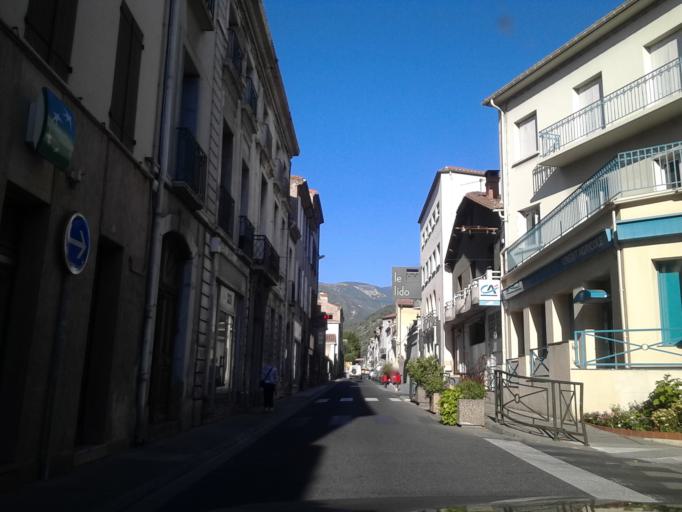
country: FR
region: Languedoc-Roussillon
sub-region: Departement des Pyrenees-Orientales
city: Prades
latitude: 42.6162
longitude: 2.4223
